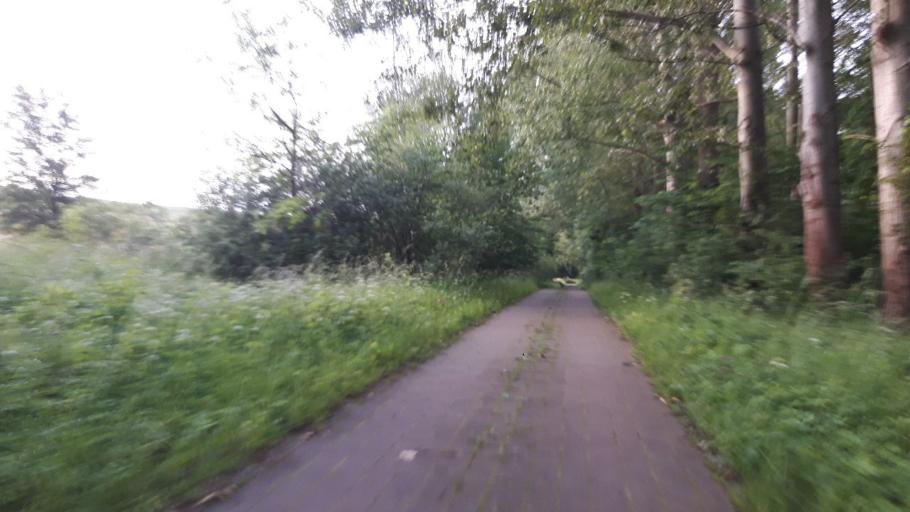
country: DE
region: Brandenburg
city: Gartz
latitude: 53.2208
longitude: 14.4064
